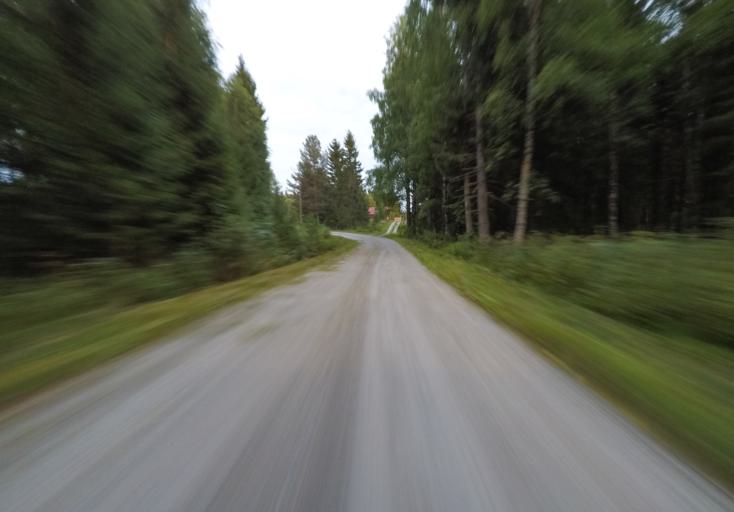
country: FI
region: Central Finland
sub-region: Jyvaeskylae
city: Hankasalmi
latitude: 62.4295
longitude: 26.6578
